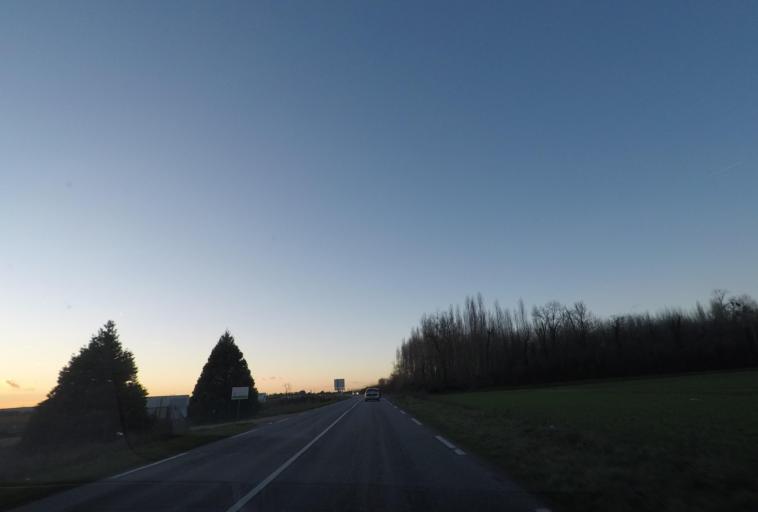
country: FR
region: Ile-de-France
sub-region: Departement de l'Essonne
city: Vert-le-Petit
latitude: 48.5692
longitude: 2.3850
